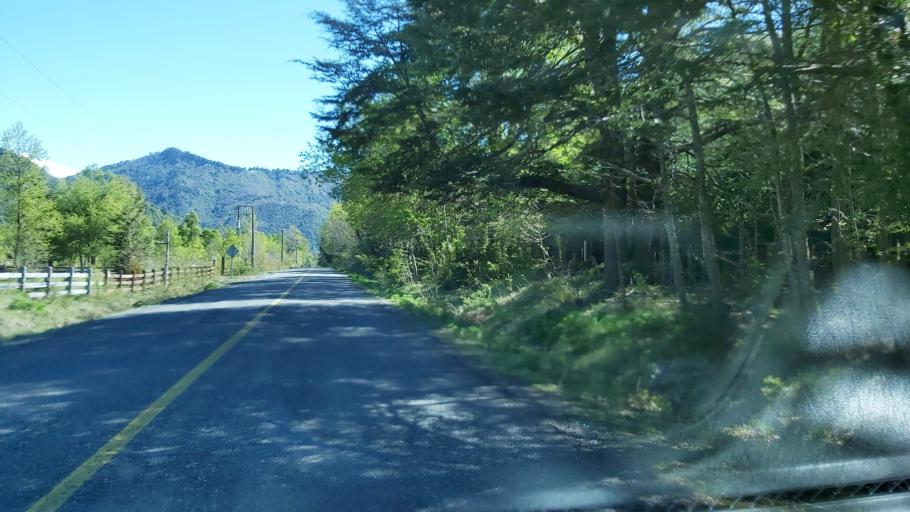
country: CL
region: Araucania
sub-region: Provincia de Cautin
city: Vilcun
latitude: -38.4737
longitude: -71.5284
